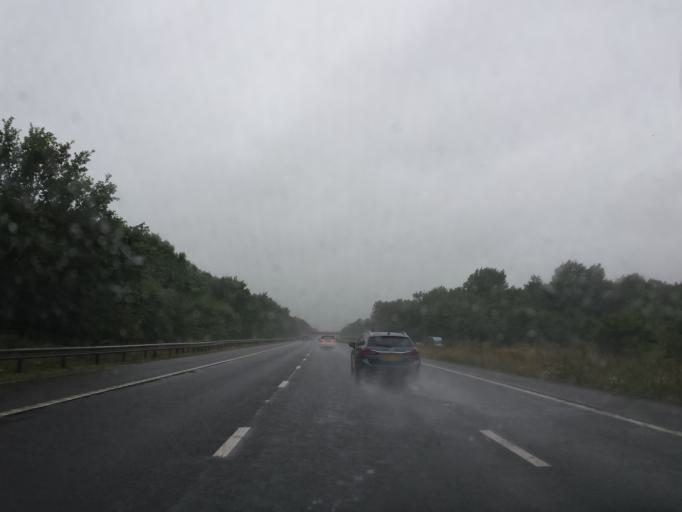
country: GB
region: England
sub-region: Leicestershire
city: Enderby
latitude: 52.5980
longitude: -1.2112
